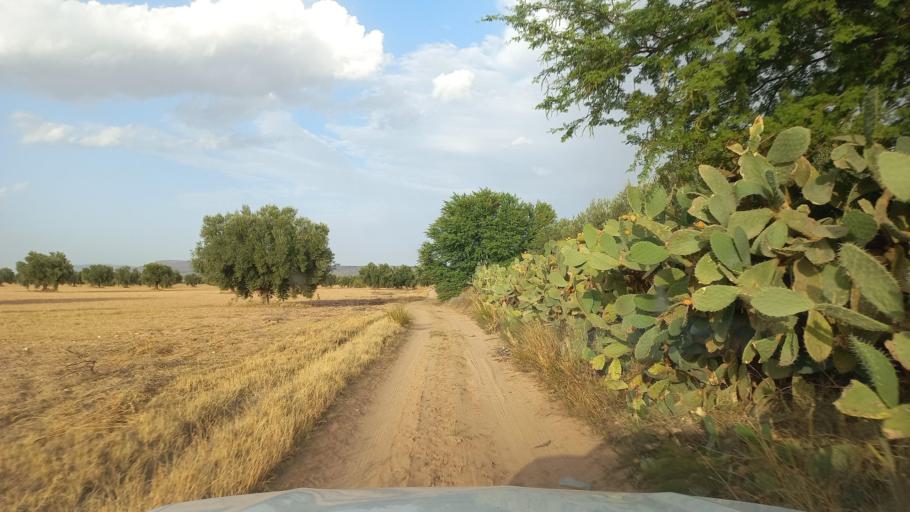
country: TN
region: Al Qasrayn
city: Kasserine
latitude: 35.2835
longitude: 9.0653
